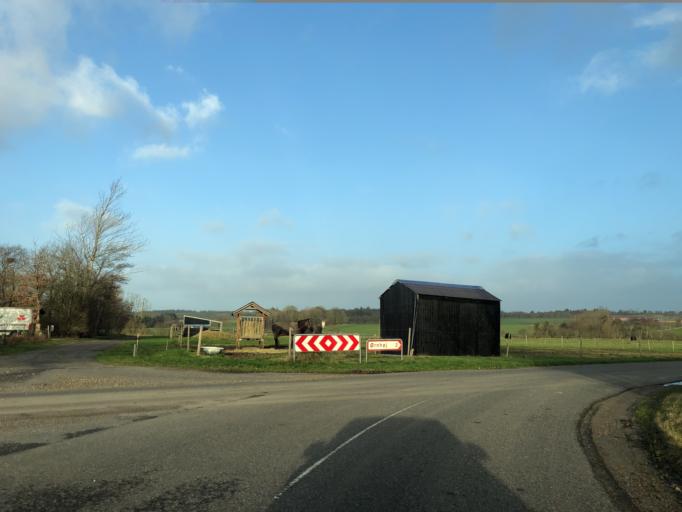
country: DK
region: Central Jutland
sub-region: Ringkobing-Skjern Kommune
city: Videbaek
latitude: 56.1941
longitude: 8.5421
